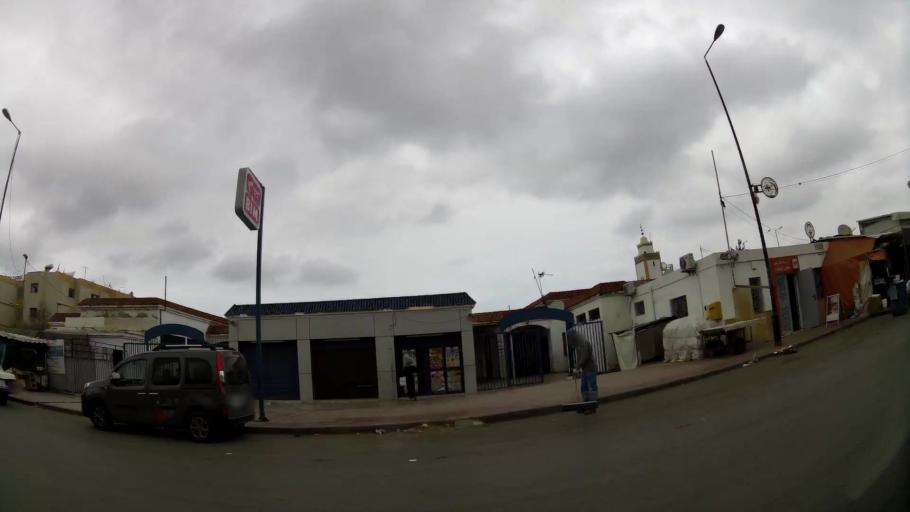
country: MA
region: Rabat-Sale-Zemmour-Zaer
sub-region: Rabat
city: Rabat
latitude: 33.9973
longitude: -6.8150
